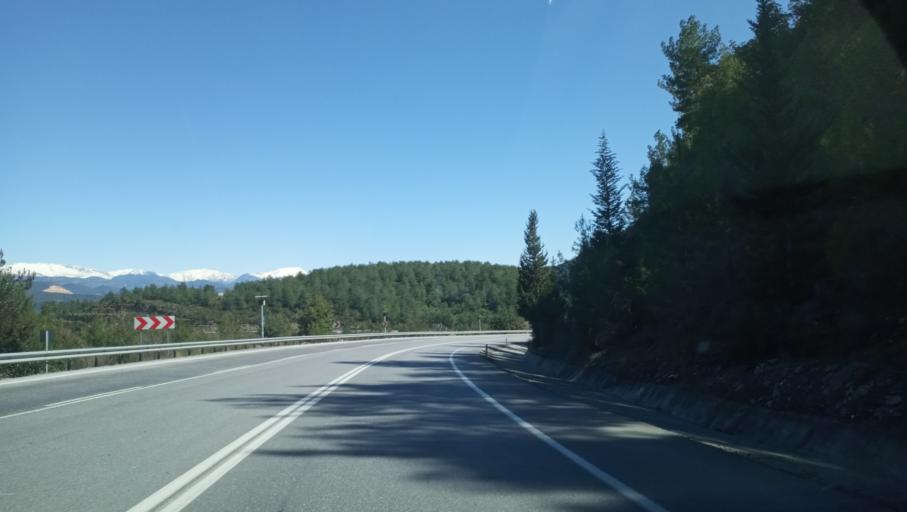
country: TR
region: Antalya
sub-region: Alanya
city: Okurcalar
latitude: 36.7690
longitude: 31.6686
